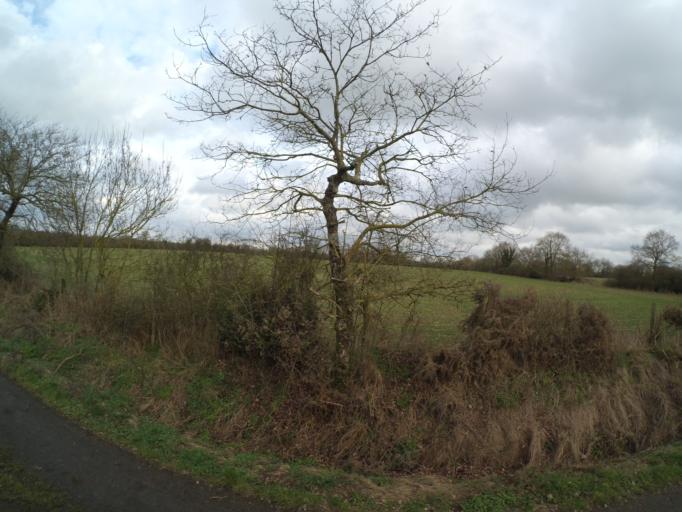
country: FR
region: Pays de la Loire
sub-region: Departement de la Vendee
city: La Bernardiere
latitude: 47.0246
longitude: -1.2923
